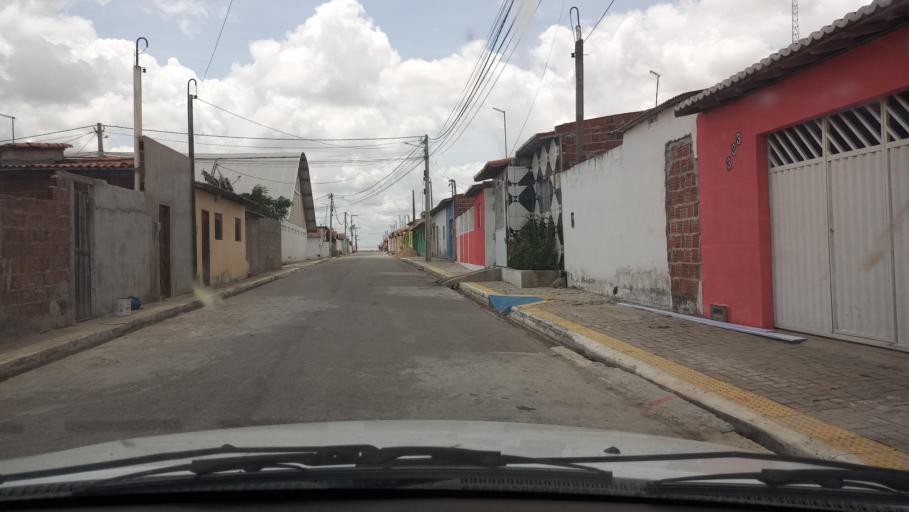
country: BR
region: Rio Grande do Norte
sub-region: Tangara
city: Tangara
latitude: -6.0956
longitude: -35.7091
